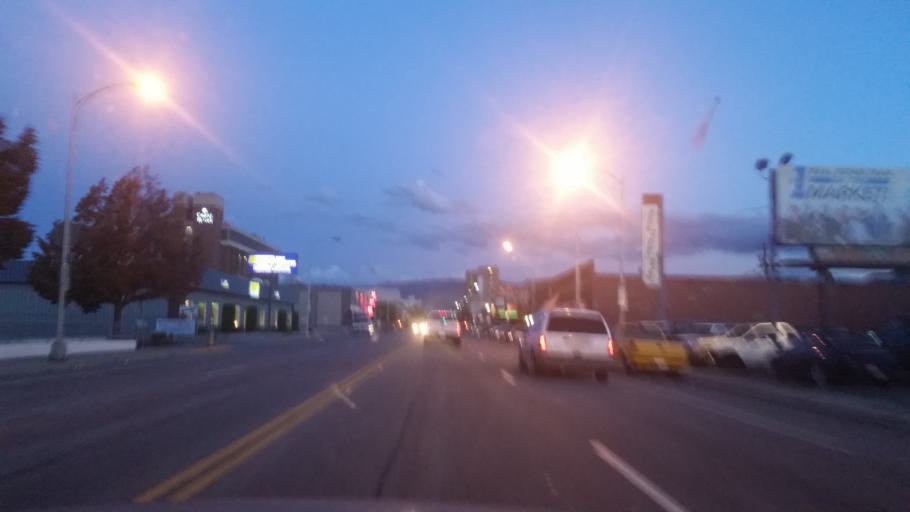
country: US
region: Washington
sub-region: Chelan County
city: Wenatchee
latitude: 47.4293
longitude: -120.3153
